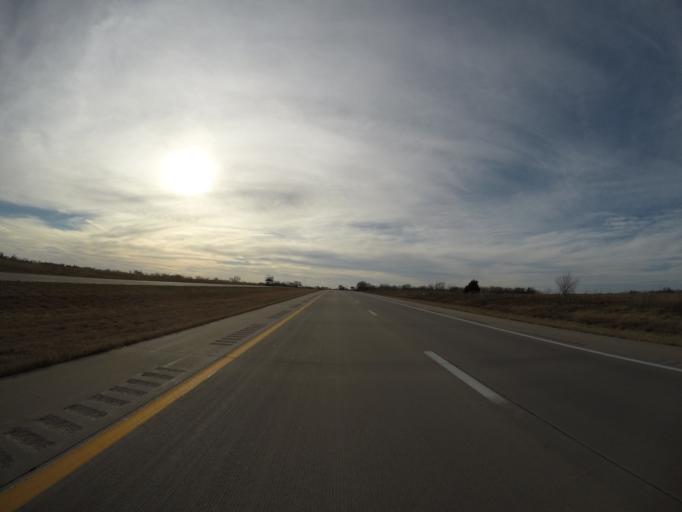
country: US
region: Kansas
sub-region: Franklin County
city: Wellsville
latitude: 38.7009
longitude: -95.0889
